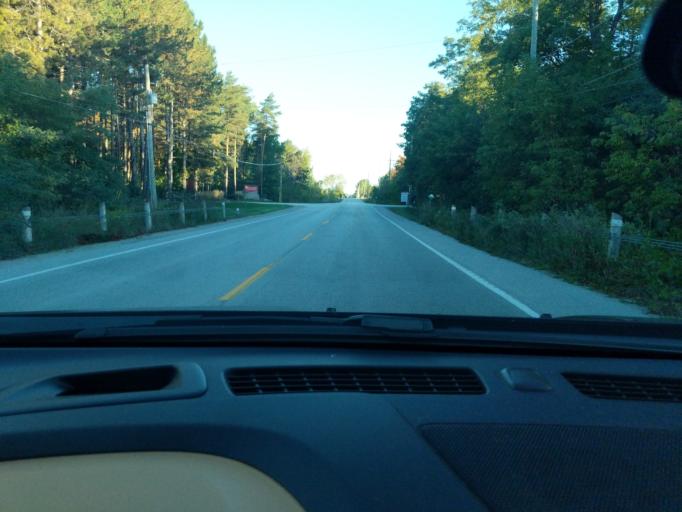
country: CA
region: Ontario
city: Collingwood
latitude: 44.5015
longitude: -80.2862
